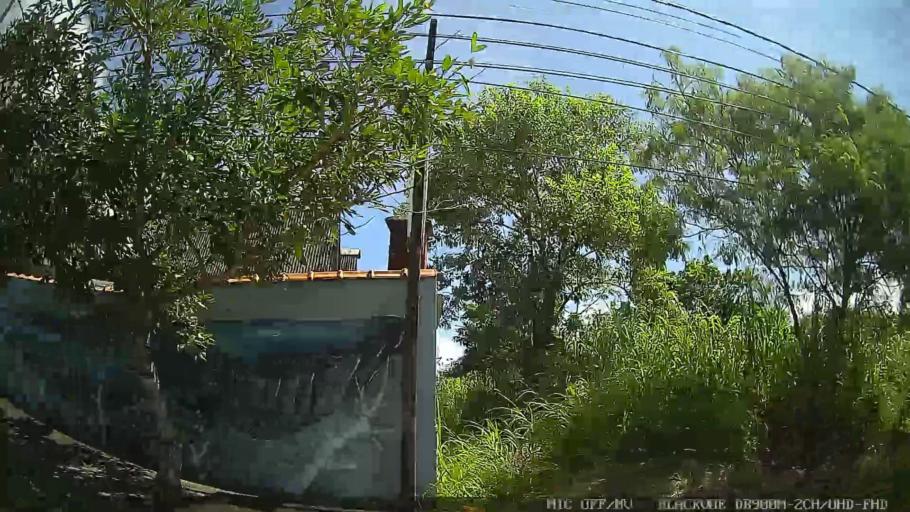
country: BR
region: Sao Paulo
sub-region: Peruibe
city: Peruibe
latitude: -24.3331
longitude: -47.0060
